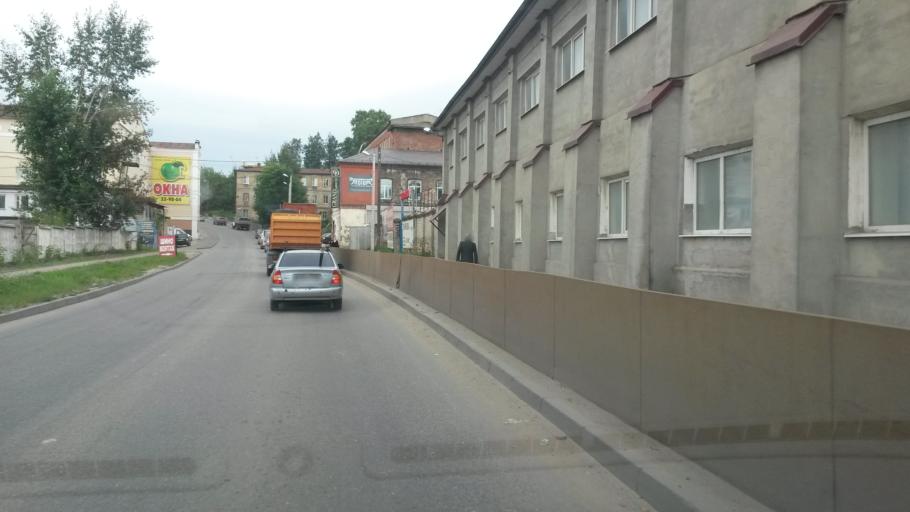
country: RU
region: Ivanovo
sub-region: Gorod Ivanovo
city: Ivanovo
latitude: 57.0129
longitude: 40.9534
